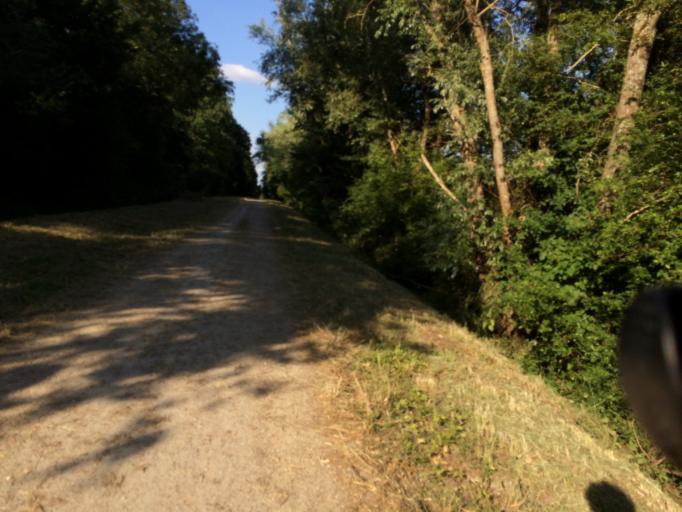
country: FR
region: Ile-de-France
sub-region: Departement de l'Essonne
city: Tigery
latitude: 48.6513
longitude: 2.4942
